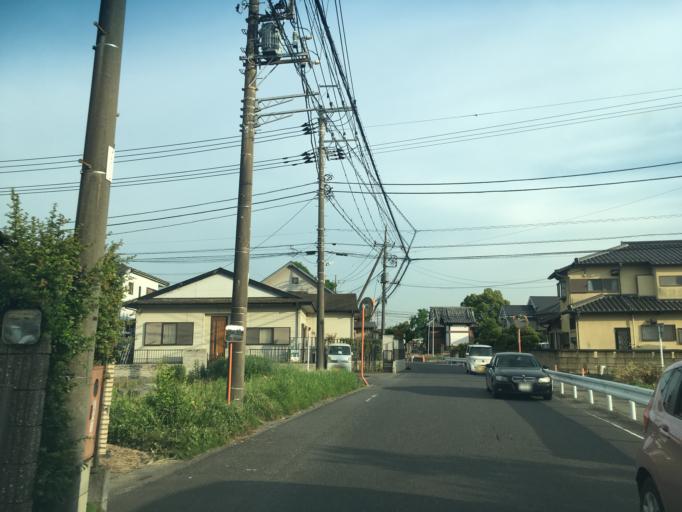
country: JP
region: Saitama
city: Yoshikawa
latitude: 35.8681
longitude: 139.8183
